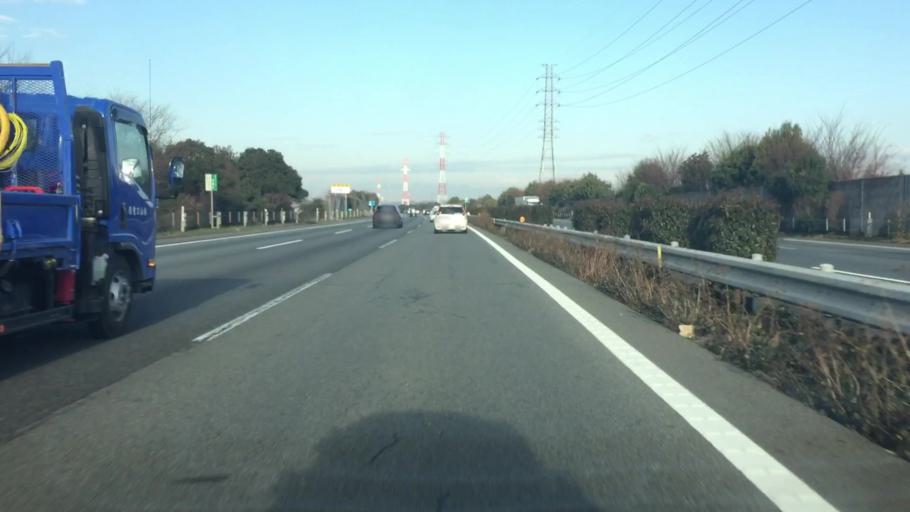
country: JP
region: Saitama
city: Yorii
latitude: 36.1554
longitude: 139.2160
